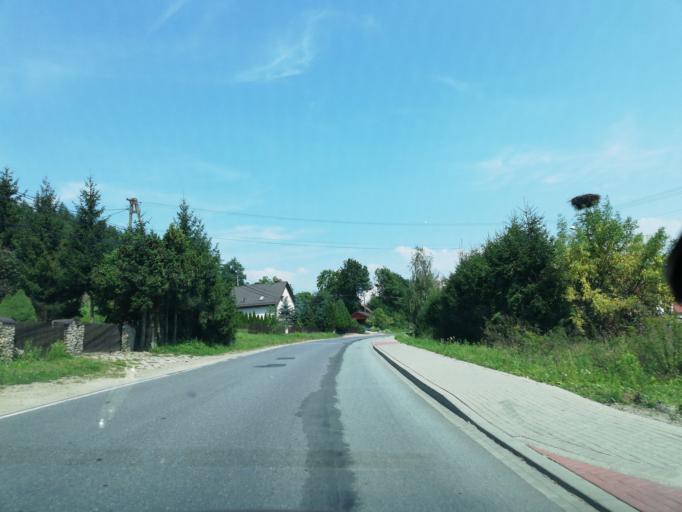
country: PL
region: Lesser Poland Voivodeship
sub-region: Powiat nowosadecki
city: Chelmiec
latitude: 49.6417
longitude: 20.6656
